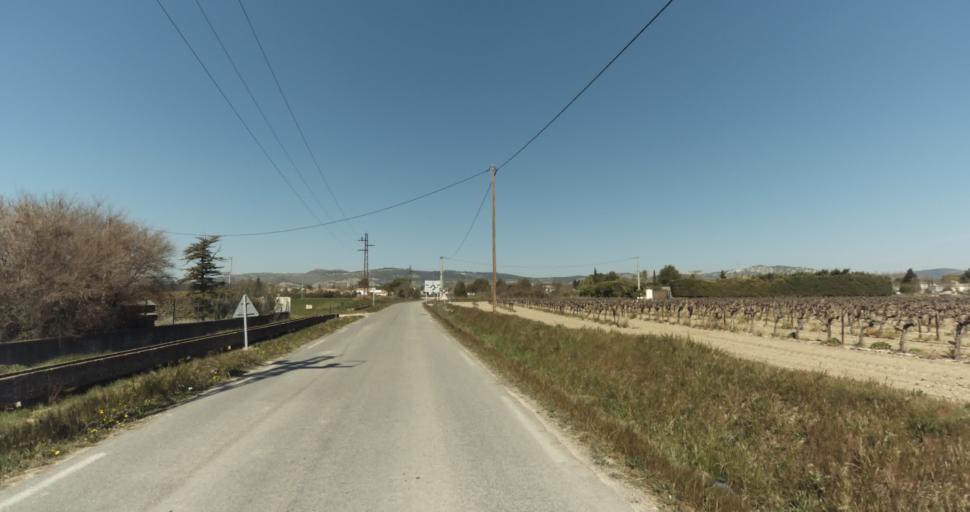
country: FR
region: Provence-Alpes-Cote d'Azur
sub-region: Departement des Bouches-du-Rhone
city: Pelissanne
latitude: 43.6237
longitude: 5.1564
